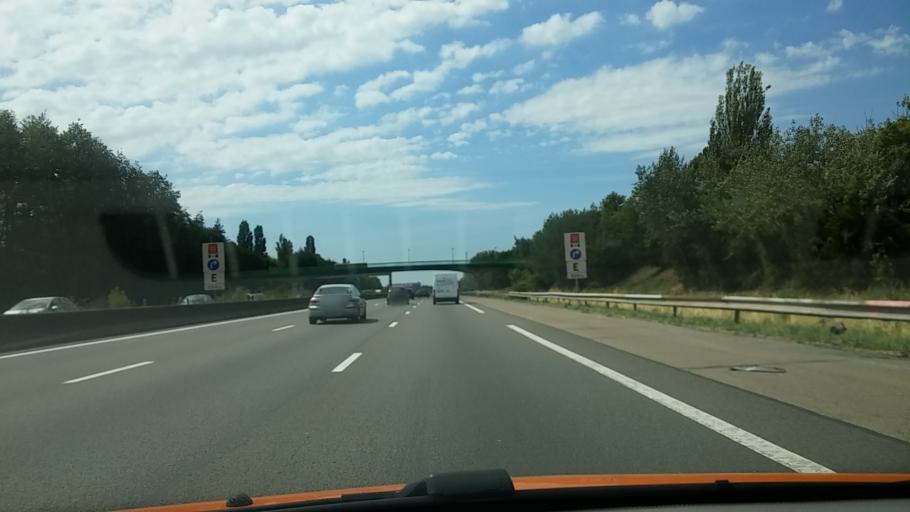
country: FR
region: Ile-de-France
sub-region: Departement du Val-de-Marne
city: Villiers-sur-Marne
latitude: 48.8361
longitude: 2.5586
